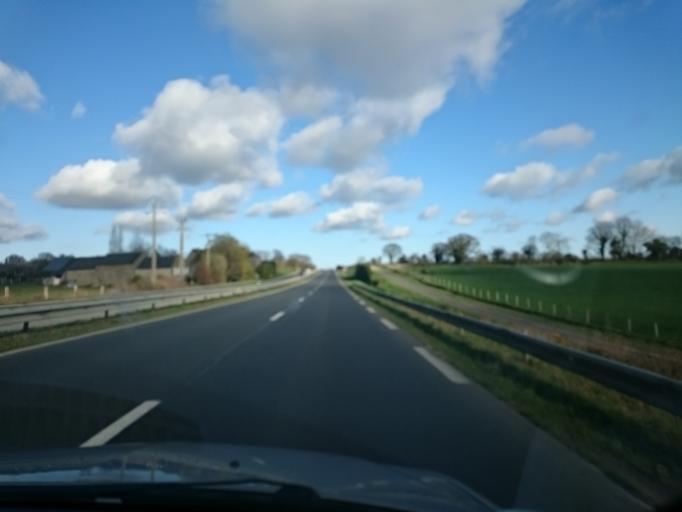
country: FR
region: Lower Normandy
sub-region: Departement de la Manche
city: Valognes
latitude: 49.4967
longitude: -1.4312
